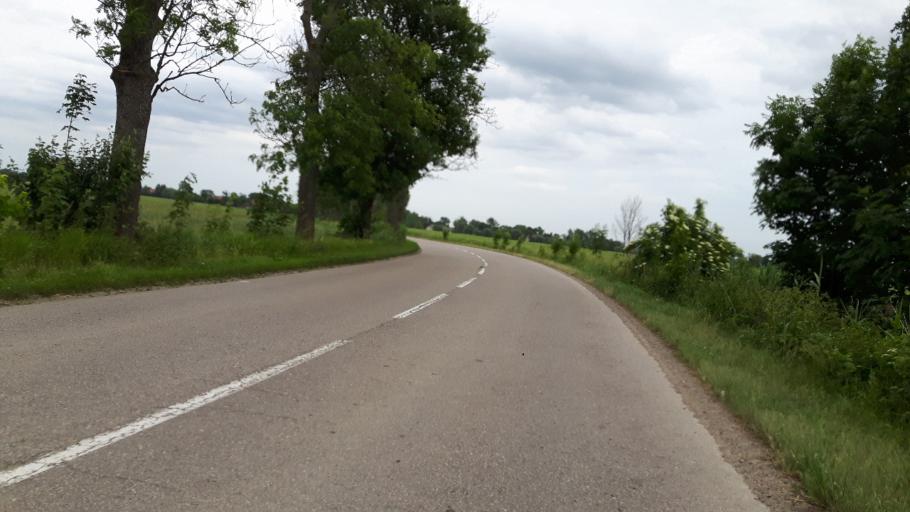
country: PL
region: Warmian-Masurian Voivodeship
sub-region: Powiat elblaski
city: Gronowo Elblaskie
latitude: 54.2068
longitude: 19.2707
